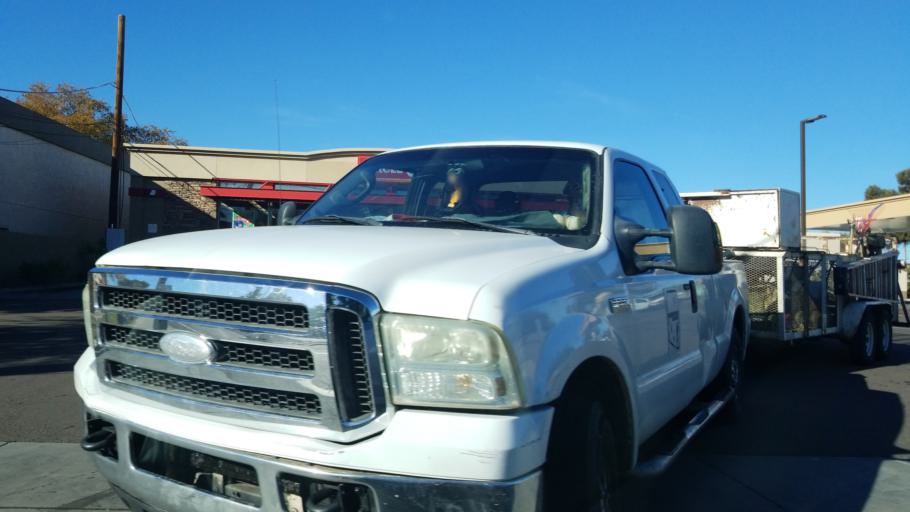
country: US
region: Arizona
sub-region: Maricopa County
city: Scottsdale
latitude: 33.5015
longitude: -111.9176
